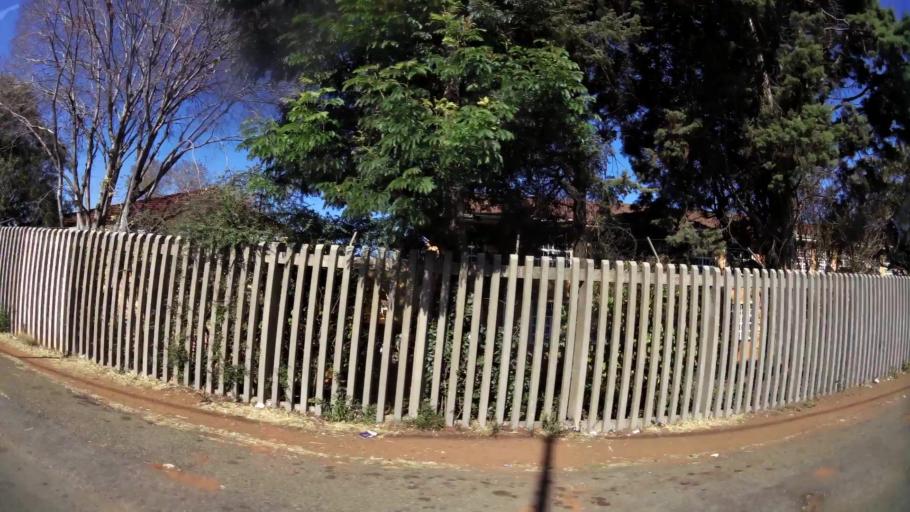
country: ZA
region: Gauteng
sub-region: City of Johannesburg Metropolitan Municipality
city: Johannesburg
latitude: -26.1920
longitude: 27.9877
